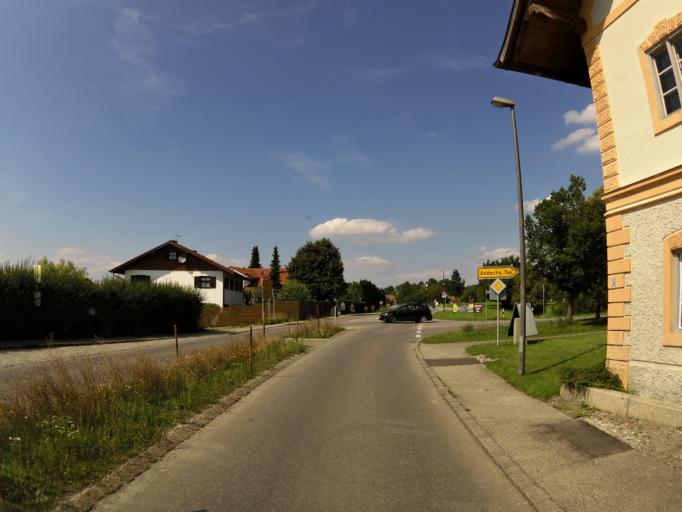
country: DE
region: Bavaria
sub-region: Upper Bavaria
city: Pahl
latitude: 47.9282
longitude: 11.1553
